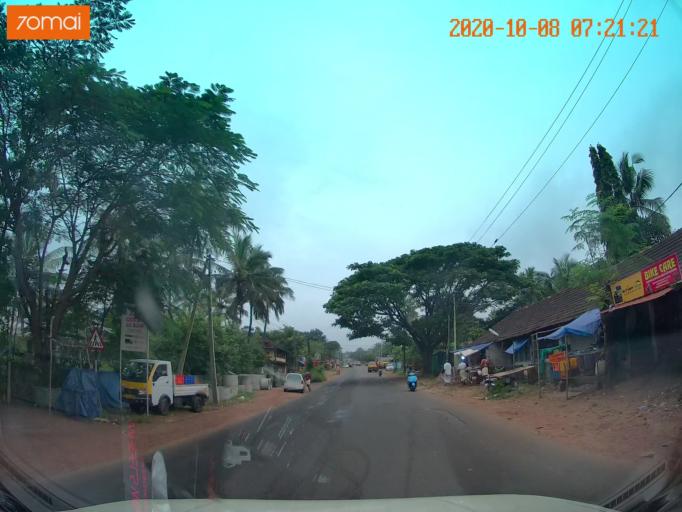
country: IN
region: Kerala
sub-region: Malappuram
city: Tirur
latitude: 10.8549
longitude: 76.0366
